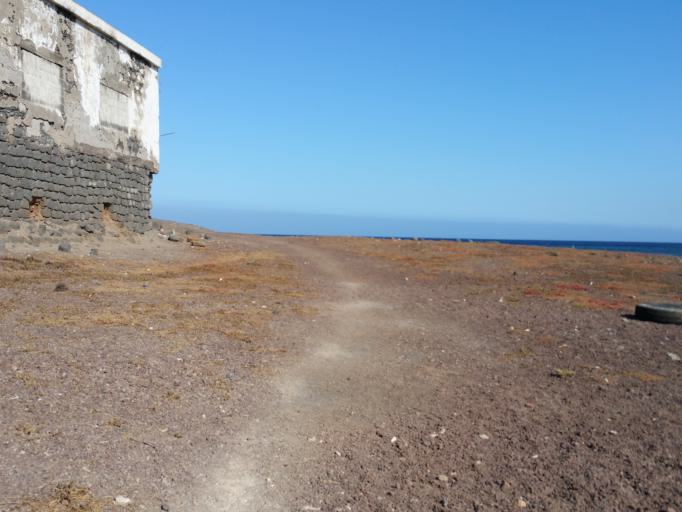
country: ES
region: Canary Islands
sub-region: Provincia de Las Palmas
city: Arrecife
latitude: 28.9593
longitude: -13.5438
